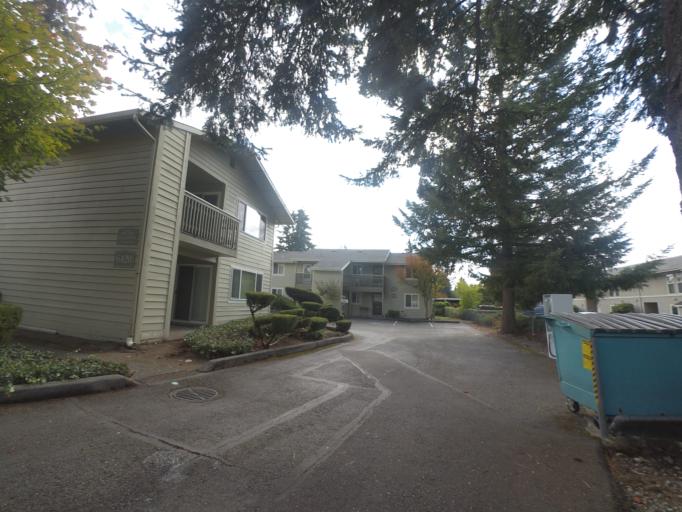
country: US
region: Washington
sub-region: Pierce County
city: Lakewood
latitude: 47.1691
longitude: -122.5237
